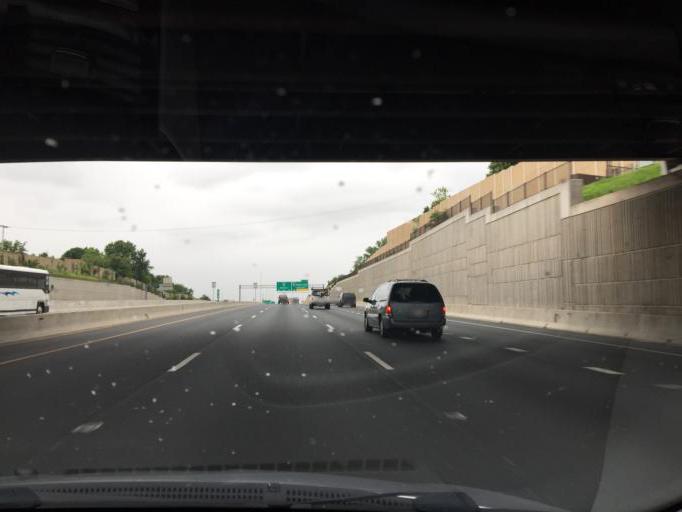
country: US
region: Maryland
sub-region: Baltimore County
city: Rosedale
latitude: 39.3307
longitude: -76.5222
